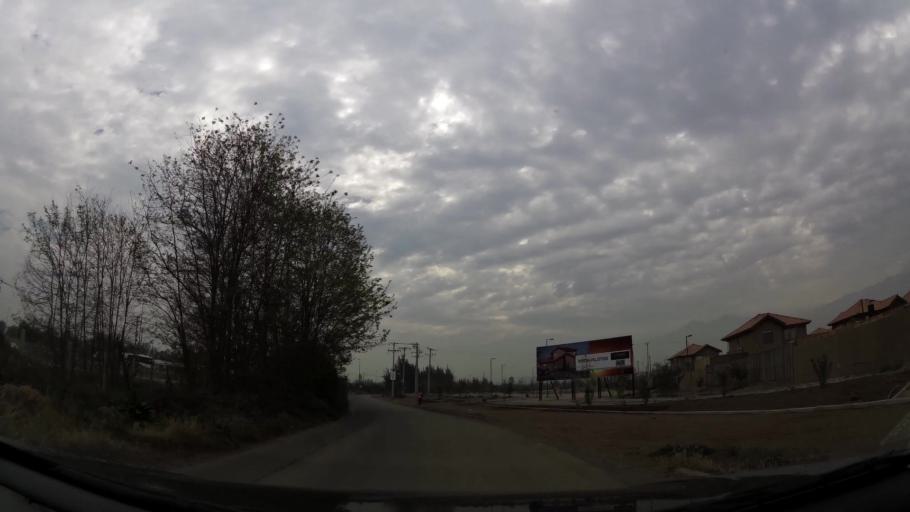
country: CL
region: Santiago Metropolitan
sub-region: Provincia de Chacabuco
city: Chicureo Abajo
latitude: -33.2190
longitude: -70.6758
